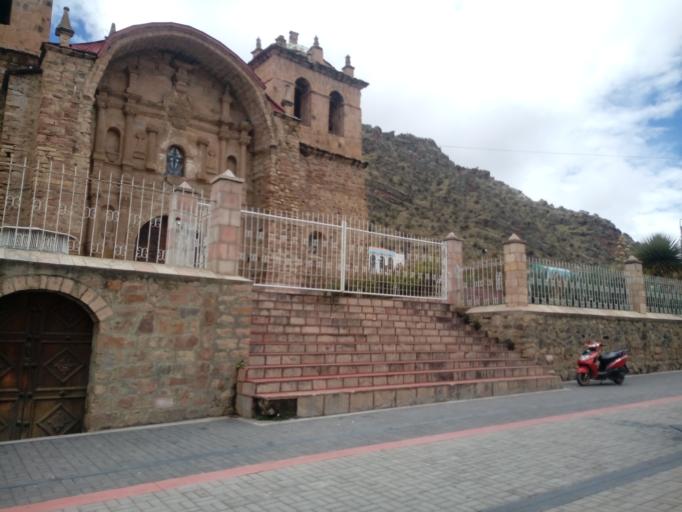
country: PE
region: Puno
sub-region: San Antonio De Putina
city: Putina
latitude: -14.9149
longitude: -69.8687
